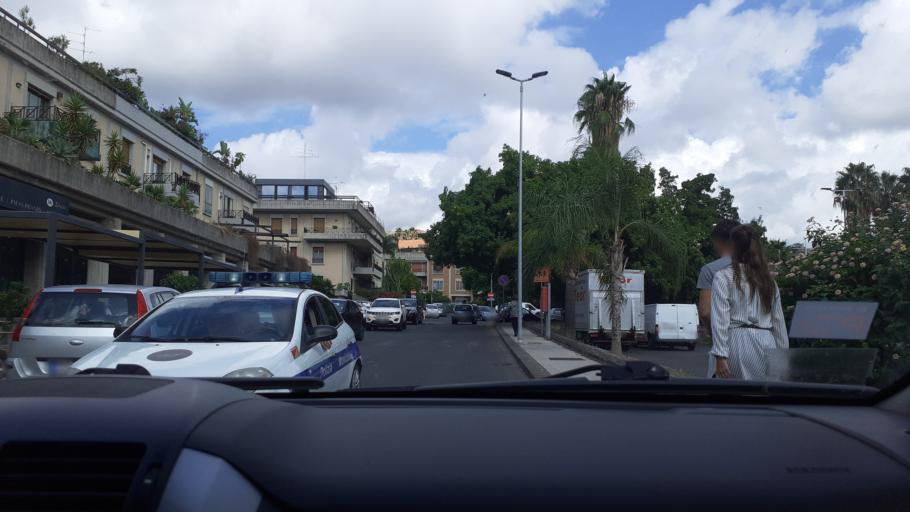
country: IT
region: Sicily
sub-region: Catania
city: Canalicchio
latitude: 37.5403
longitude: 15.0991
